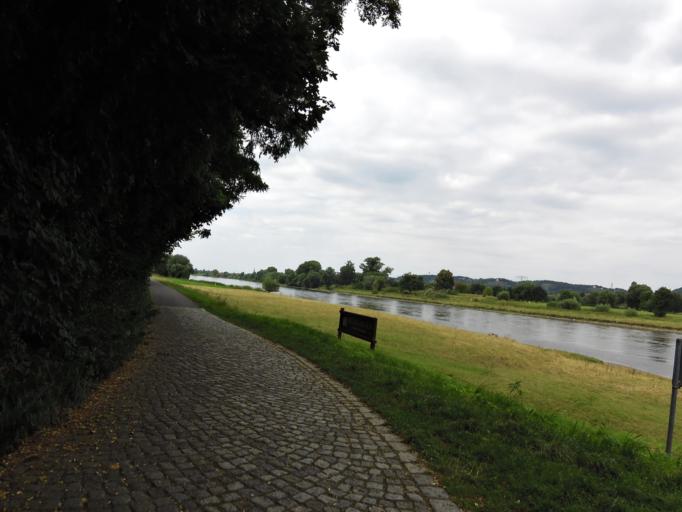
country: DE
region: Saxony
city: Radebeul
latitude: 51.0904
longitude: 13.6578
